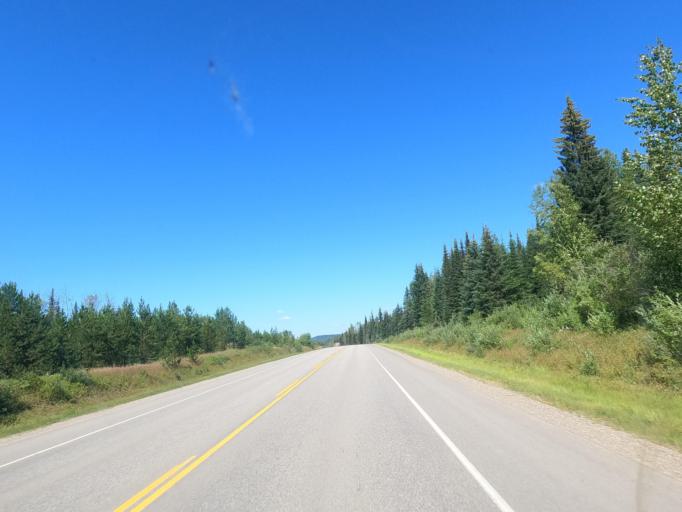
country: CA
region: British Columbia
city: Prince George
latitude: 54.2133
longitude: -122.6033
